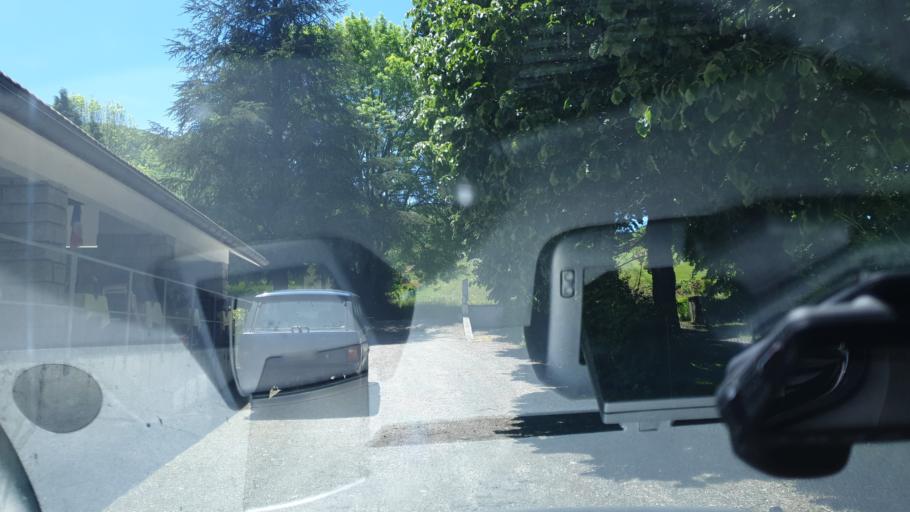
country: FR
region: Midi-Pyrenees
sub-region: Departement de l'Ariege
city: Saint-Girons
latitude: 42.8914
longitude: 1.3430
